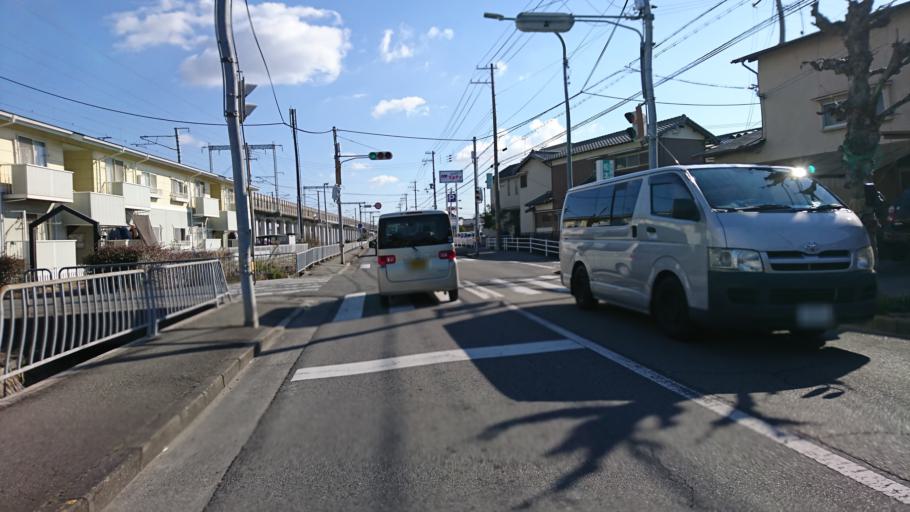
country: JP
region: Hyogo
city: Kakogawacho-honmachi
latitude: 34.7730
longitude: 134.7910
